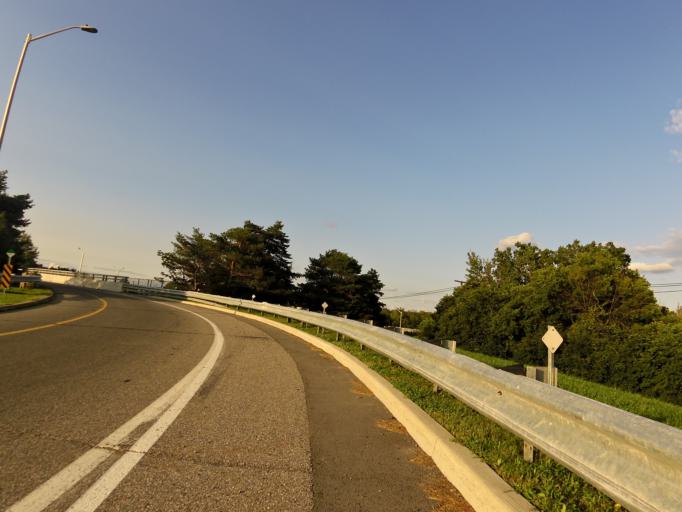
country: CA
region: Ontario
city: Ottawa
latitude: 45.3768
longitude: -75.6817
